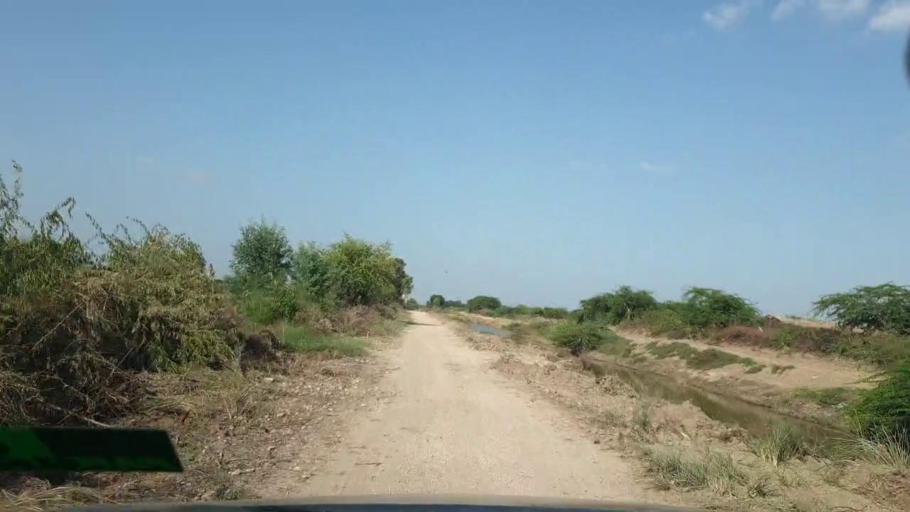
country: PK
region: Sindh
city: Naukot
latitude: 24.7103
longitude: 69.2059
